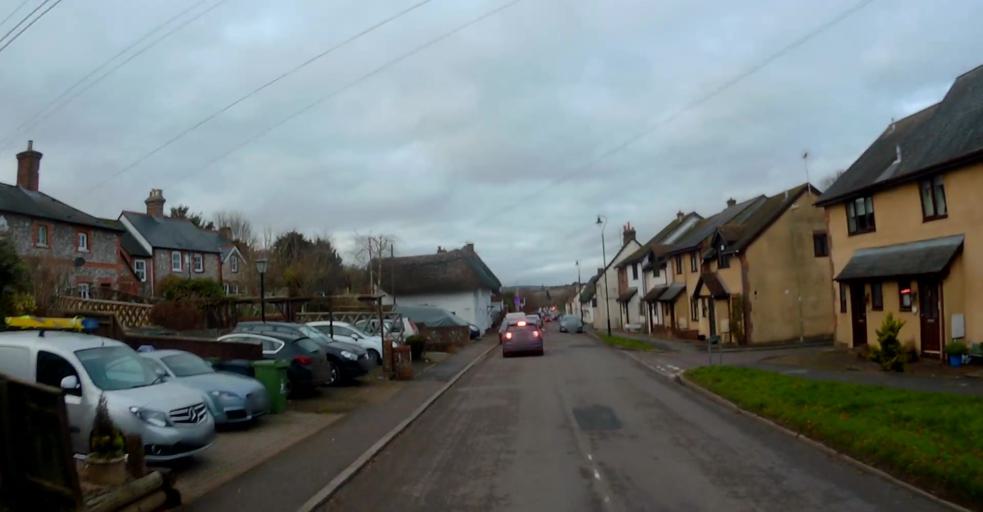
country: GB
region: England
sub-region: Hampshire
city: Overton
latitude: 51.2403
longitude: -1.2620
